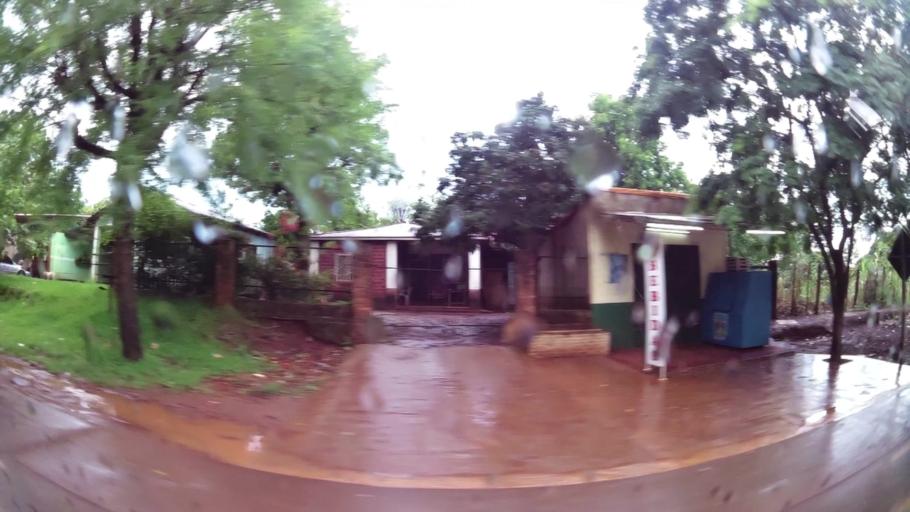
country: PY
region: Alto Parana
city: Presidente Franco
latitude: -25.5582
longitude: -54.6610
